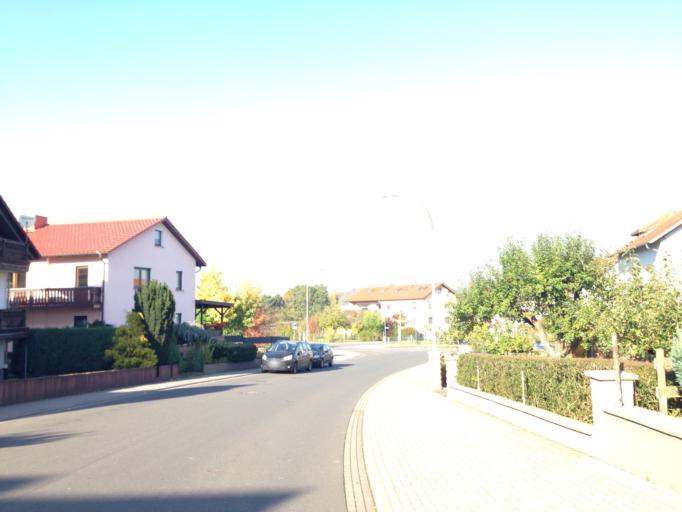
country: DE
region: Hesse
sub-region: Regierungsbezirk Giessen
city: Reiskirchen
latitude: 50.5770
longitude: 8.8143
